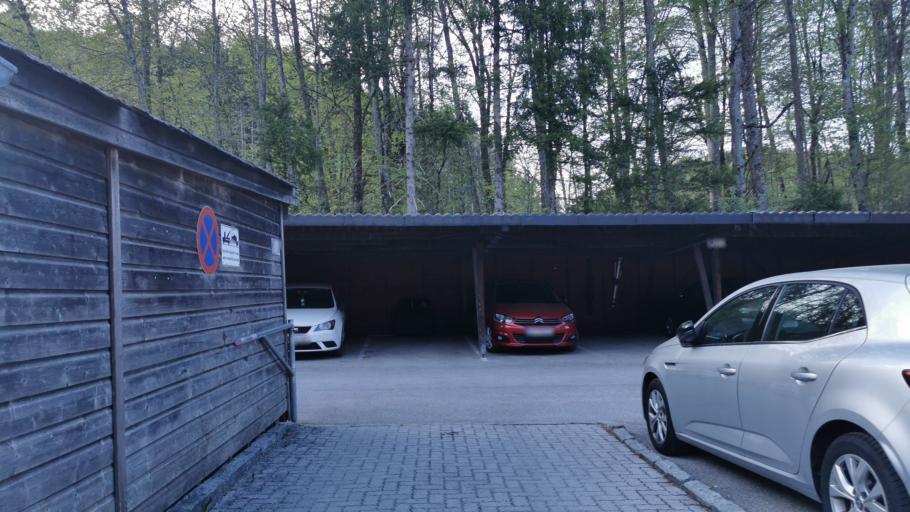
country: AT
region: Salzburg
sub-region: Politischer Bezirk Salzburg-Umgebung
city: Grodig
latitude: 47.7494
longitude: 12.9932
